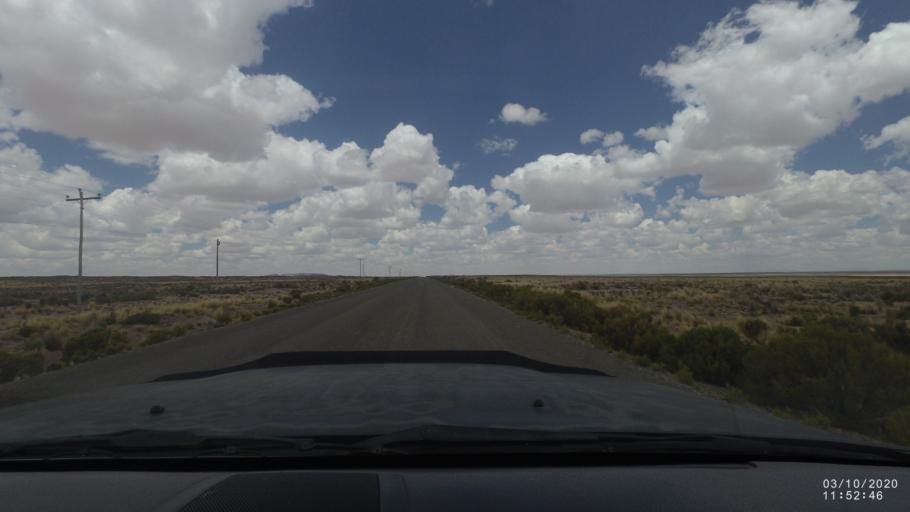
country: BO
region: Oruro
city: Poopo
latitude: -18.4664
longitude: -67.6012
